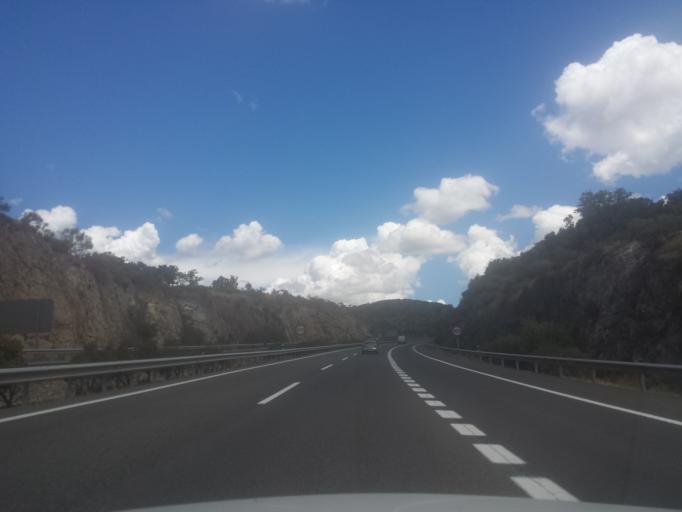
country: ES
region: Extremadura
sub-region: Provincia de Caceres
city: Aldeanueva del Camino
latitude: 40.2713
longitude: -5.9127
